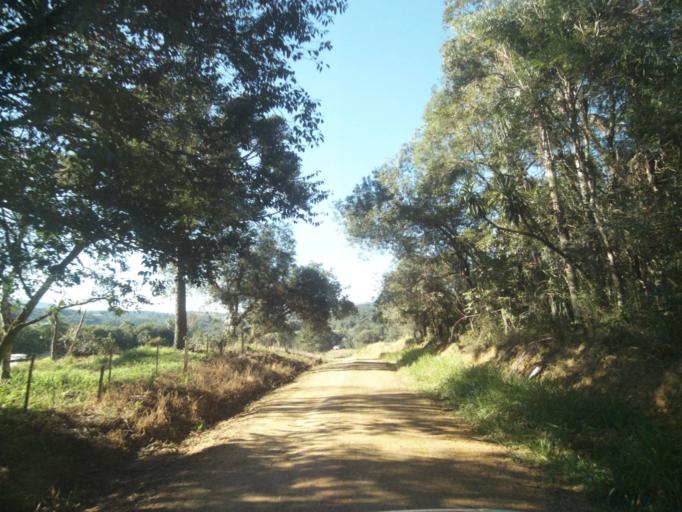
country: BR
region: Parana
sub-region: Tibagi
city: Tibagi
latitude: -24.5533
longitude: -50.5213
